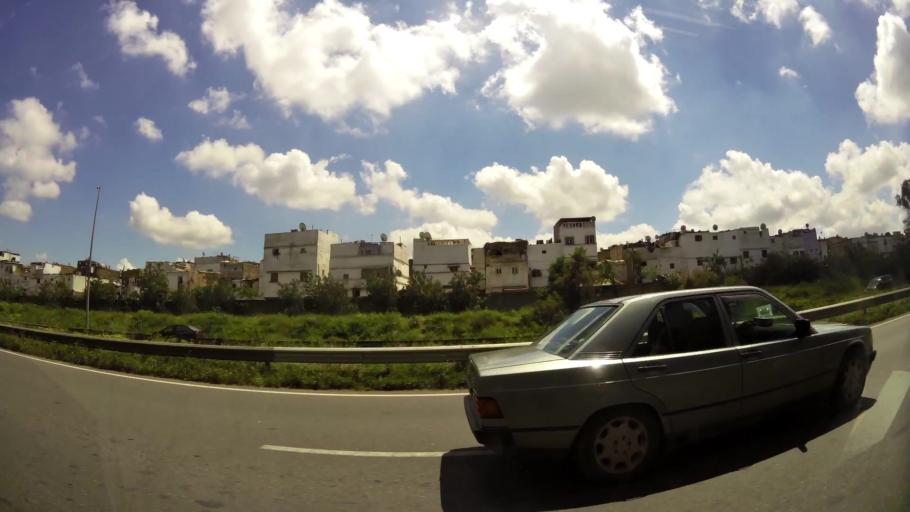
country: MA
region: Grand Casablanca
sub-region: Casablanca
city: Casablanca
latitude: 33.5220
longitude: -7.5762
